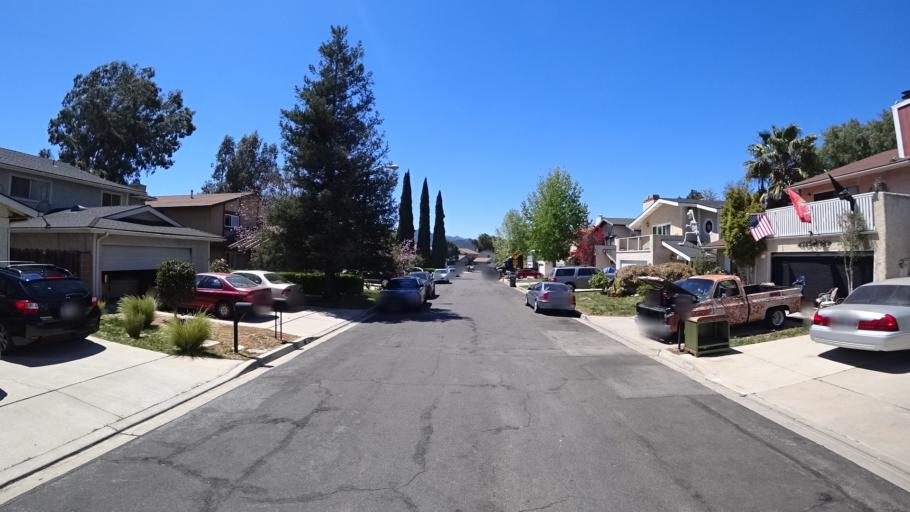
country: US
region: California
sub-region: Ventura County
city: Thousand Oaks
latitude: 34.1850
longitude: -118.8638
